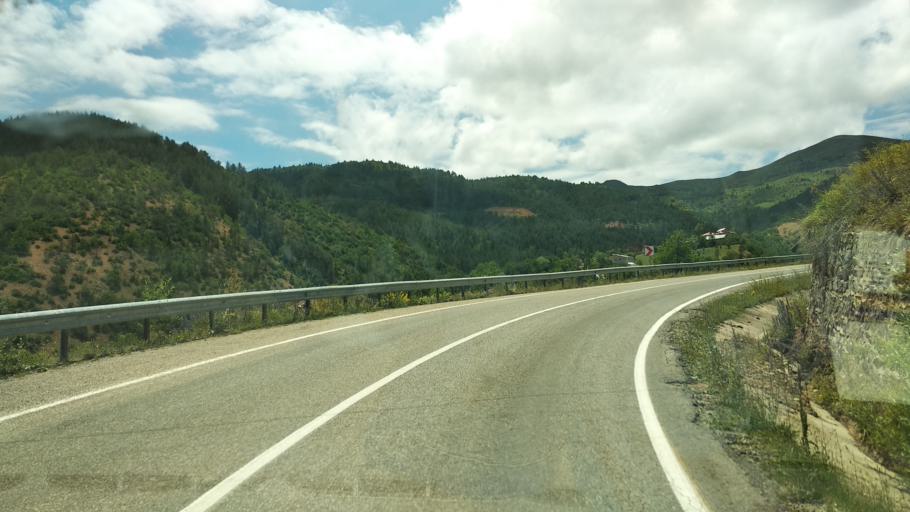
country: TR
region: Gumushane
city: Kose
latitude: 40.3070
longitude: 39.5584
